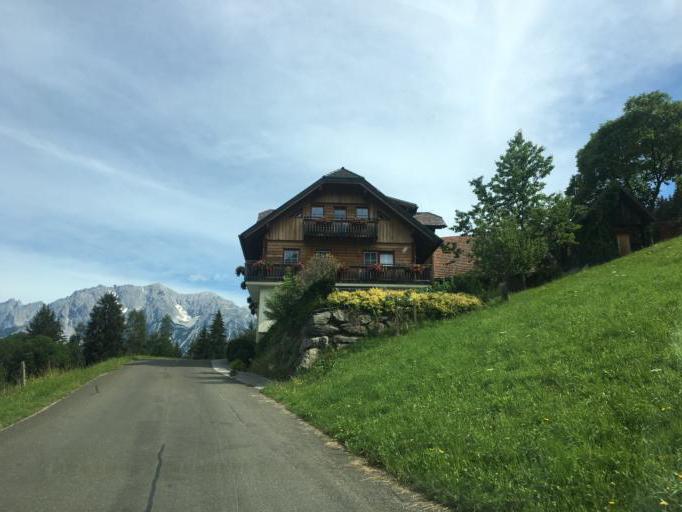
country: AT
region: Styria
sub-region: Politischer Bezirk Liezen
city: Schladming
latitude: 47.3748
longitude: 13.6781
